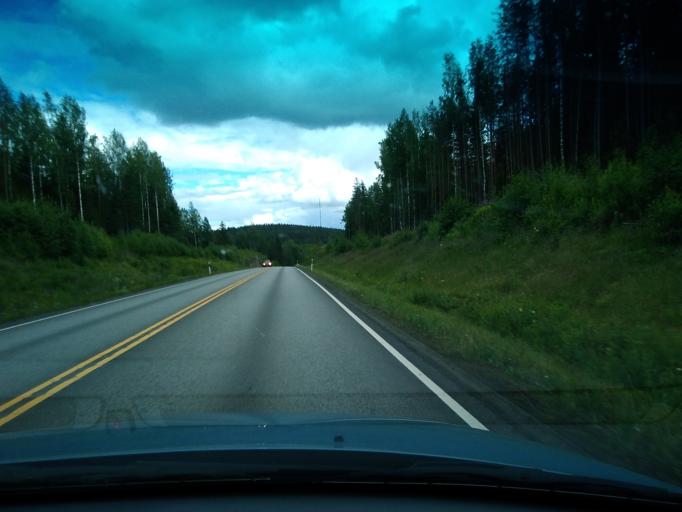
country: FI
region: Central Finland
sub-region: Saarijaervi-Viitasaari
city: Saarijaervi
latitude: 62.7182
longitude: 25.2219
